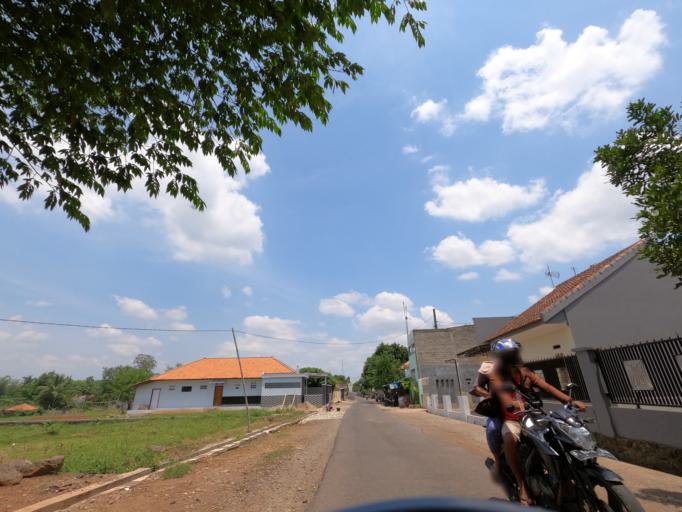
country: ID
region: West Java
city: Pamanukan
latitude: -6.5206
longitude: 107.7768
